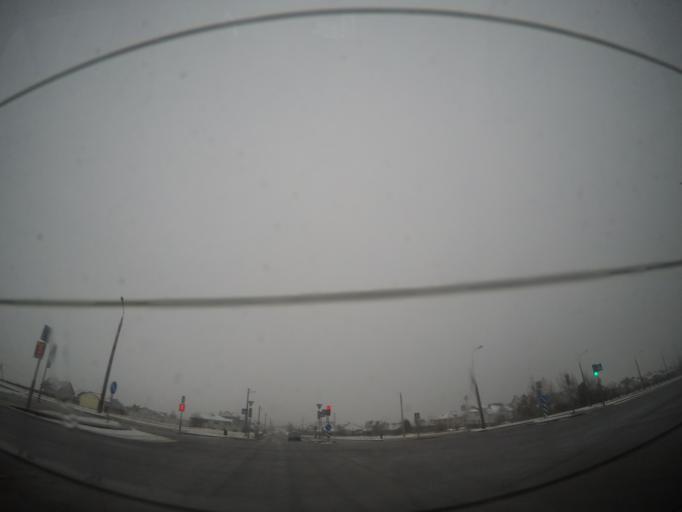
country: BY
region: Grodnenskaya
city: Hrodna
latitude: 53.6212
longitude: 23.8219
